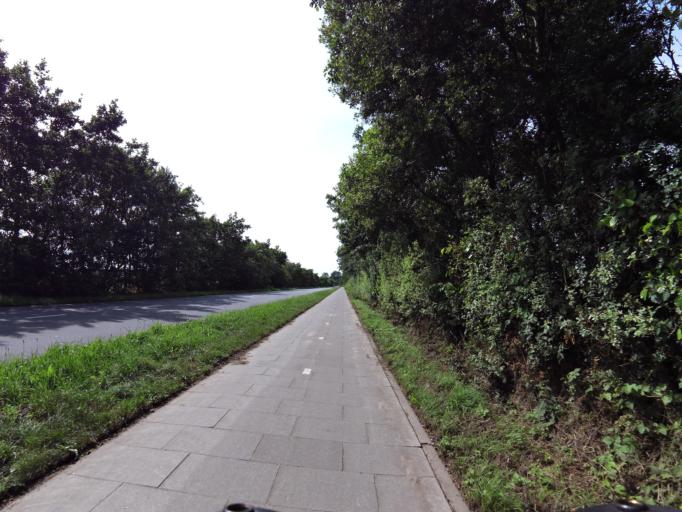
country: NL
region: Zeeland
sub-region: Schouwen-Duiveland
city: Burgh
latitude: 51.7131
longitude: 3.7214
